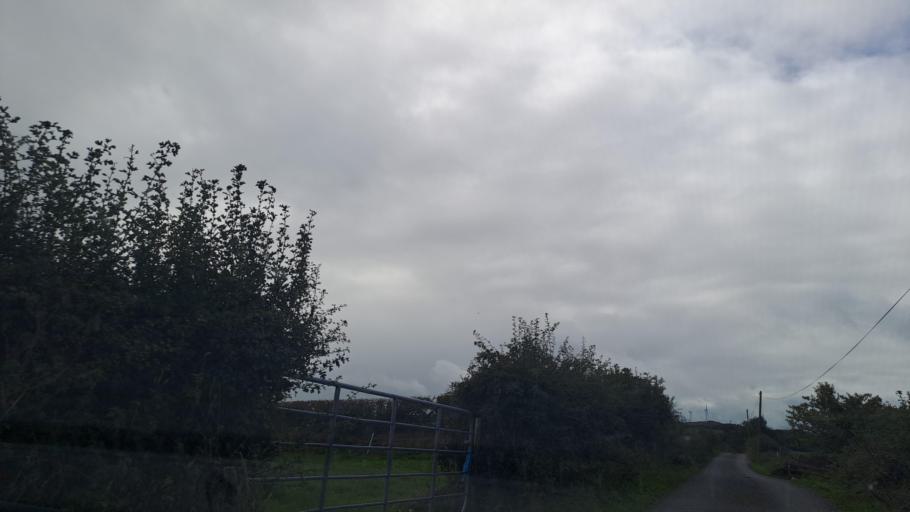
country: IE
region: Ulster
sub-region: An Cabhan
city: Kingscourt
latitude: 53.9782
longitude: -6.8416
